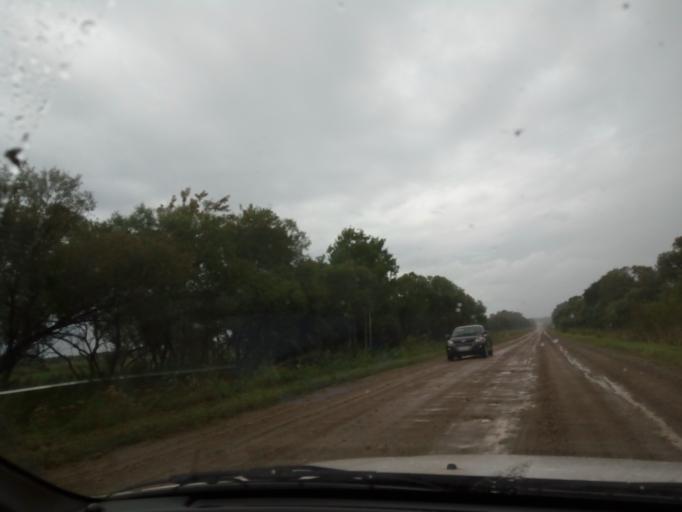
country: RU
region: Primorskiy
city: Lazo
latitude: 45.8450
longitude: 133.6446
